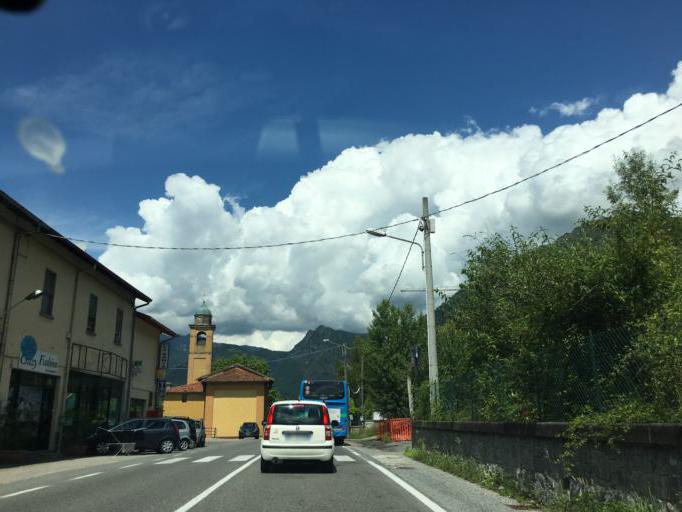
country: IT
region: Lombardy
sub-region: Provincia di Como
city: Bene Lario
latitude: 46.0329
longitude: 9.1905
